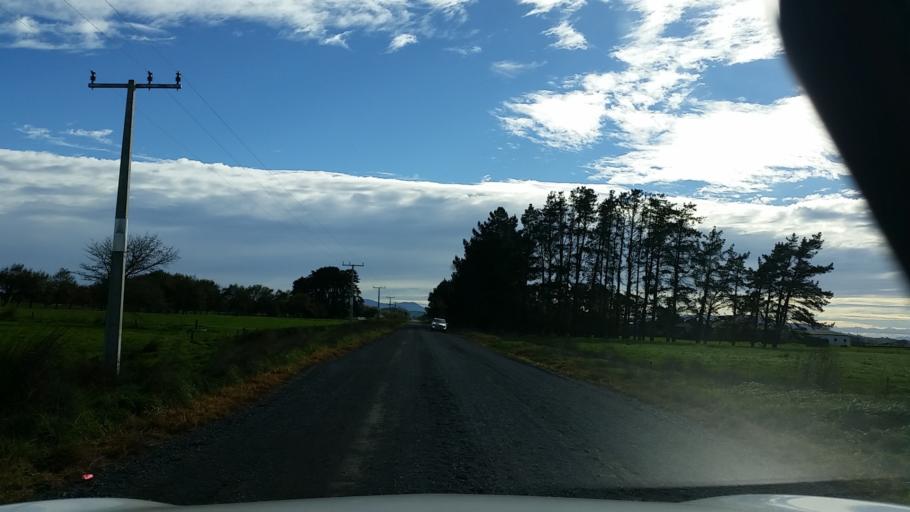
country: NZ
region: Waikato
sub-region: Hamilton City
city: Hamilton
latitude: -37.6599
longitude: 175.4370
